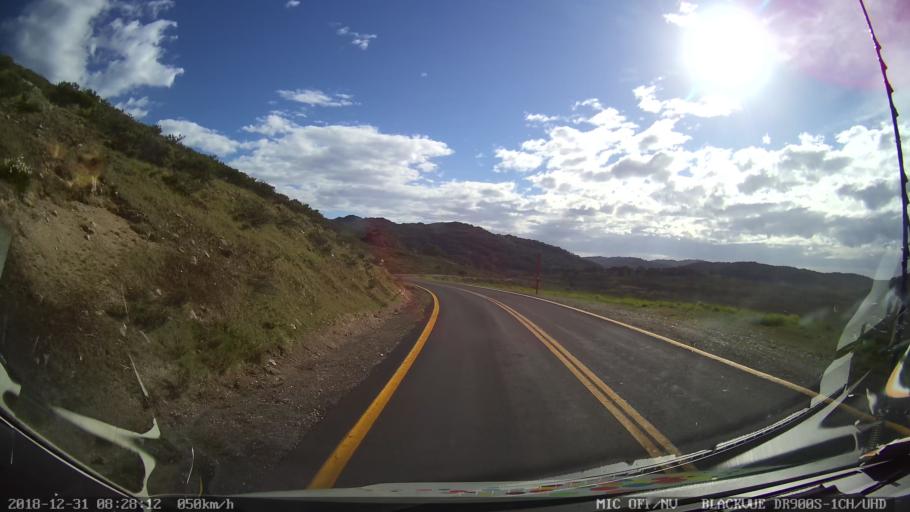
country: AU
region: New South Wales
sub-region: Snowy River
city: Jindabyne
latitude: -36.4298
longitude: 148.3441
